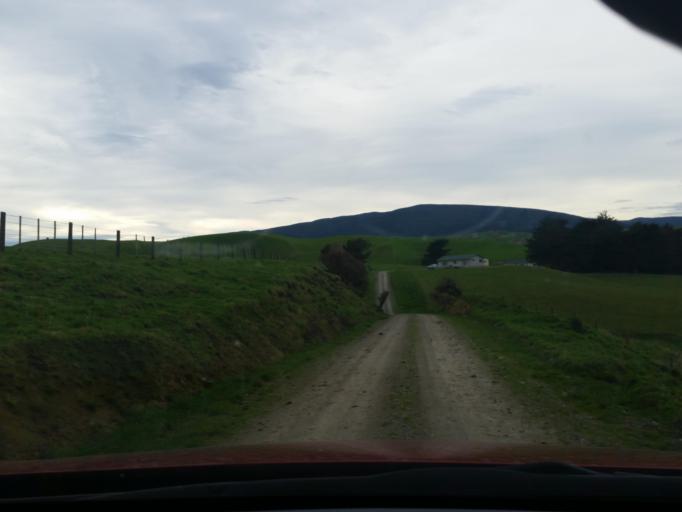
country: NZ
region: Southland
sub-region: Southland District
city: Riverton
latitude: -46.1833
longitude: 167.6850
